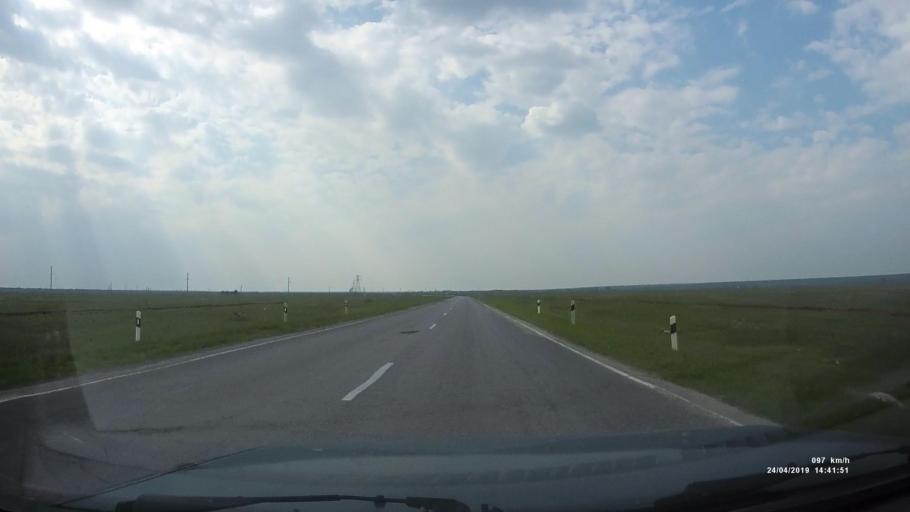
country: RU
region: Rostov
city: Remontnoye
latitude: 46.4485
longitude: 43.8732
